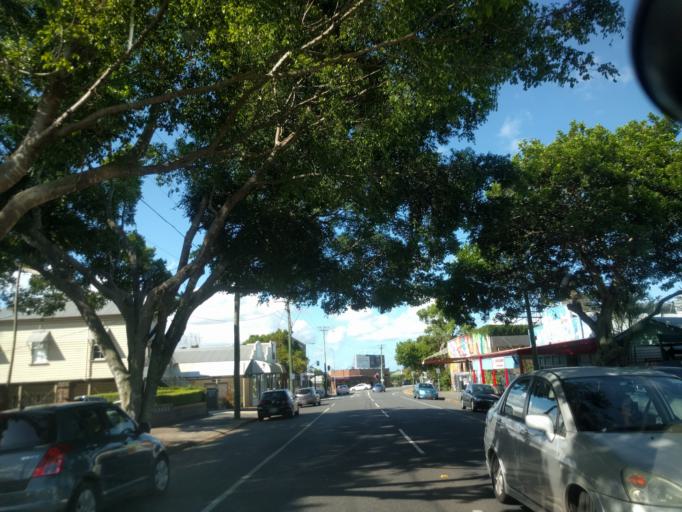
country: AU
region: Queensland
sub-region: Brisbane
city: Milton
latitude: -27.4534
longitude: 153.0037
